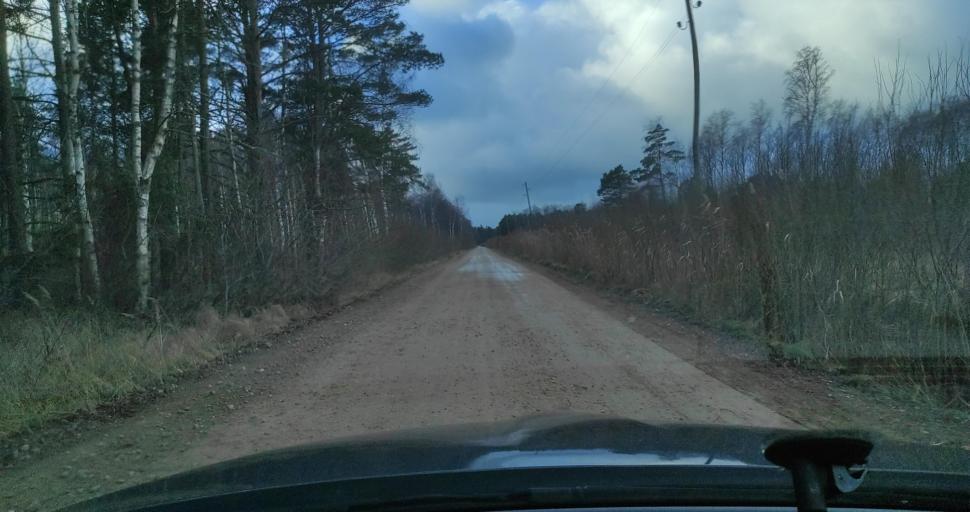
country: LV
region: Pavilostas
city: Pavilosta
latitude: 56.8572
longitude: 21.1496
